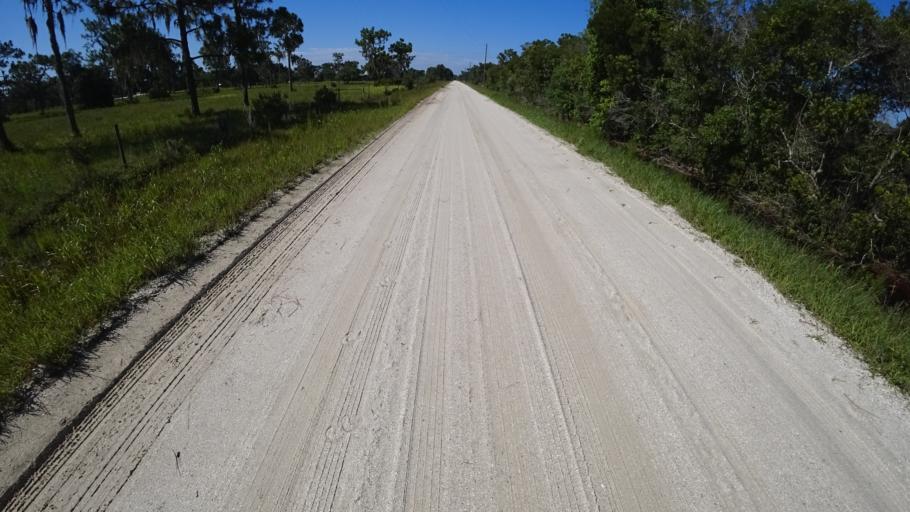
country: US
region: Florida
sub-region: Sarasota County
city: The Meadows
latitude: 27.4096
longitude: -82.2875
